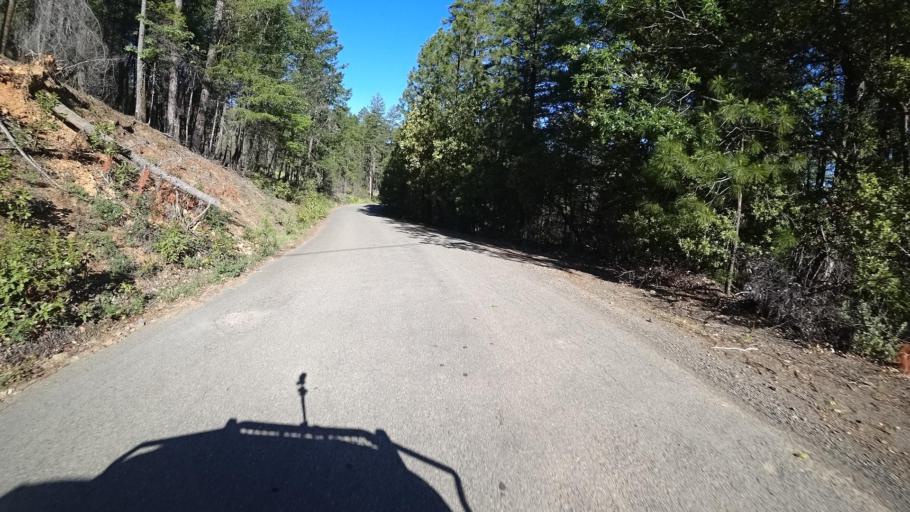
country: US
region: California
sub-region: Lake County
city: Upper Lake
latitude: 39.4018
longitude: -122.9590
